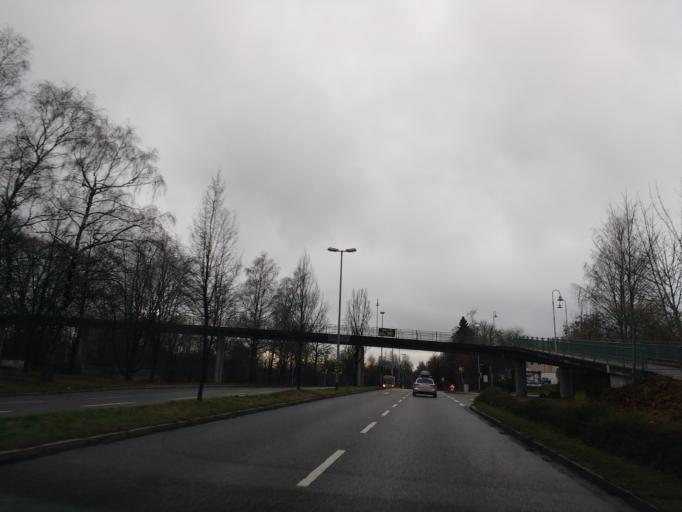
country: DE
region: Bavaria
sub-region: Swabia
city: Kempten (Allgaeu)
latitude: 47.7188
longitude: 10.3310
